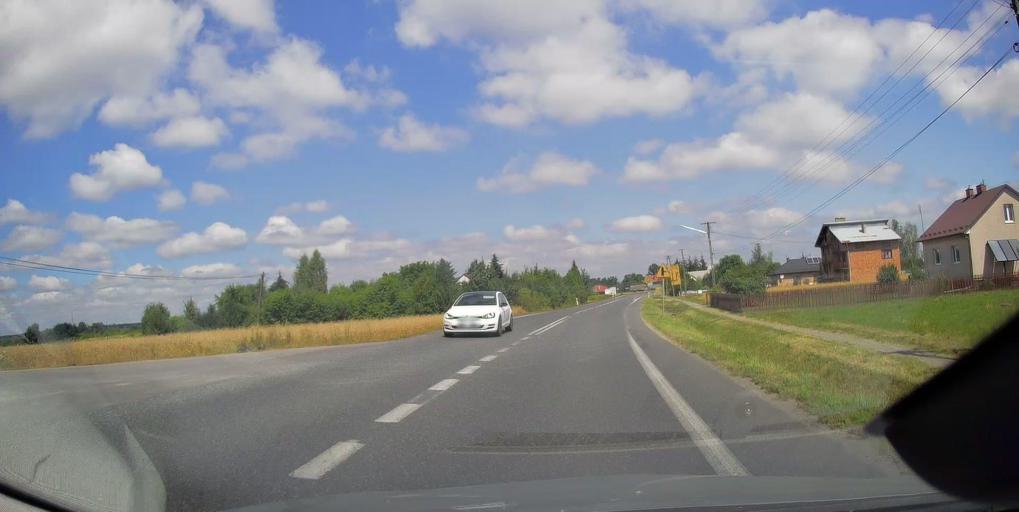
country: PL
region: Subcarpathian Voivodeship
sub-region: Powiat mielecki
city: Przeclaw
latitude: 50.1513
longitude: 21.4833
